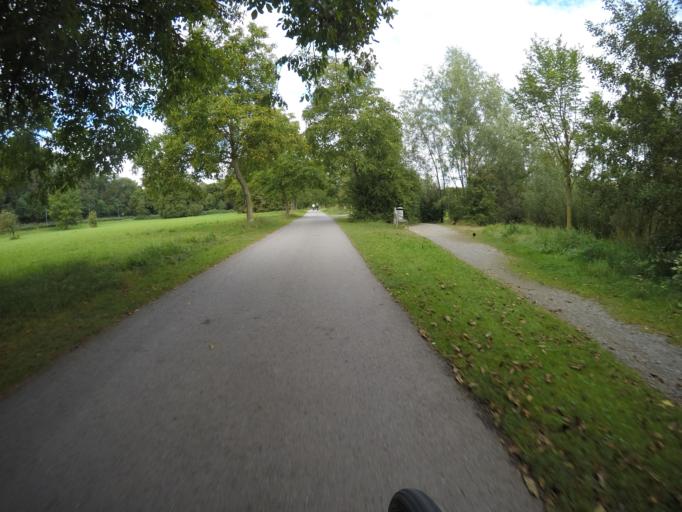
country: DE
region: Baden-Wuerttemberg
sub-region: Regierungsbezirk Stuttgart
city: Freiberg am Neckar
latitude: 48.9092
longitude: 9.2185
